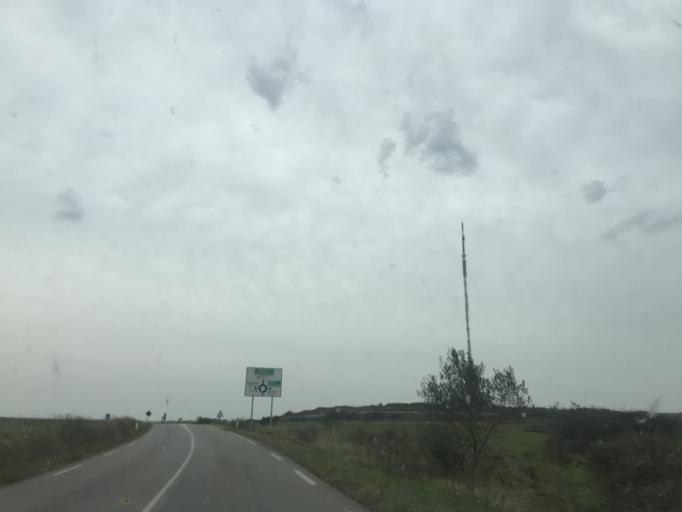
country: FR
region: Brittany
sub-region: Departement du Finistere
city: Plouneour-Menez
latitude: 48.4097
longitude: -3.8971
